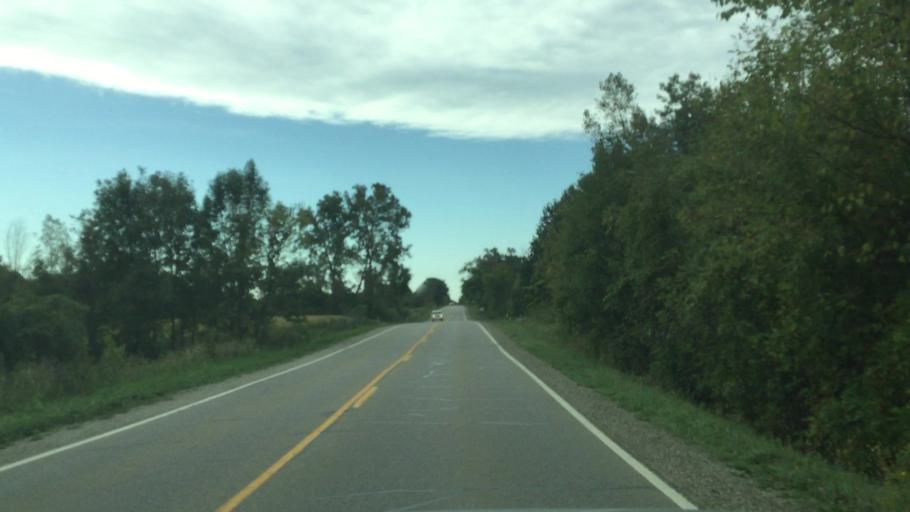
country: US
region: Michigan
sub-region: Livingston County
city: Howell
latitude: 42.6459
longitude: -83.8761
